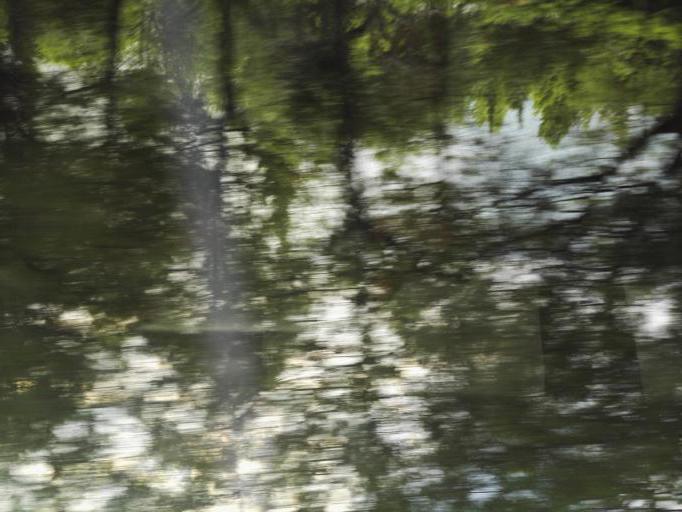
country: IT
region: Calabria
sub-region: Provincia di Reggio Calabria
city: Bova Marina
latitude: 37.9271
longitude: 15.9353
